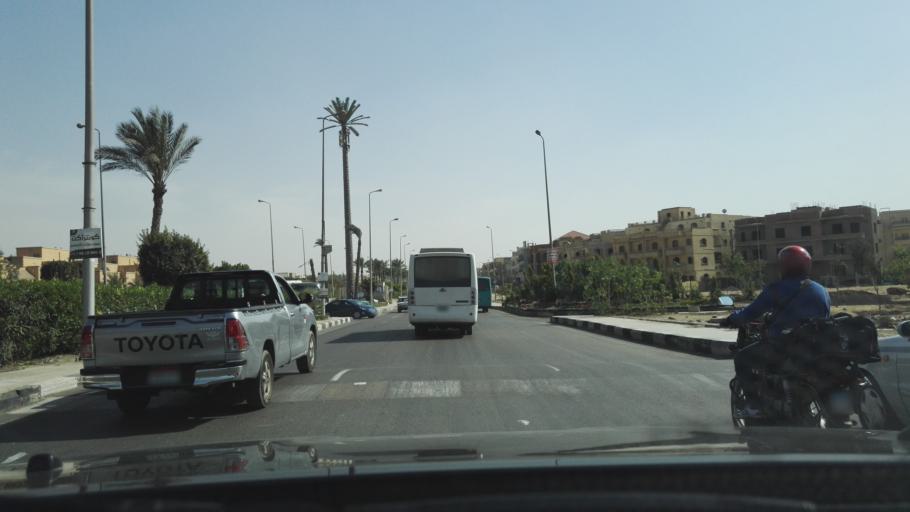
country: EG
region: Muhafazat al Qalyubiyah
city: Al Khankah
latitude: 30.0600
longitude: 31.4749
